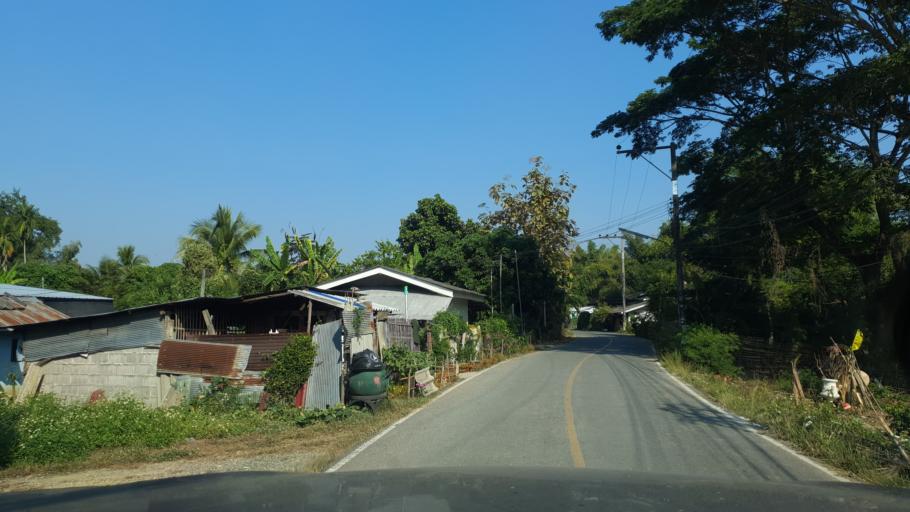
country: TH
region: Chiang Mai
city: Saraphi
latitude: 18.7062
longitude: 99.0755
